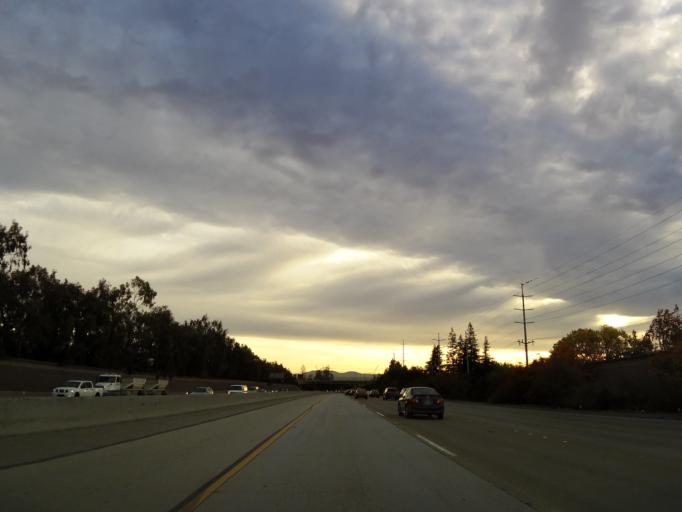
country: US
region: California
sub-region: Santa Clara County
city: Cupertino
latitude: 37.3343
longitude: -122.0274
